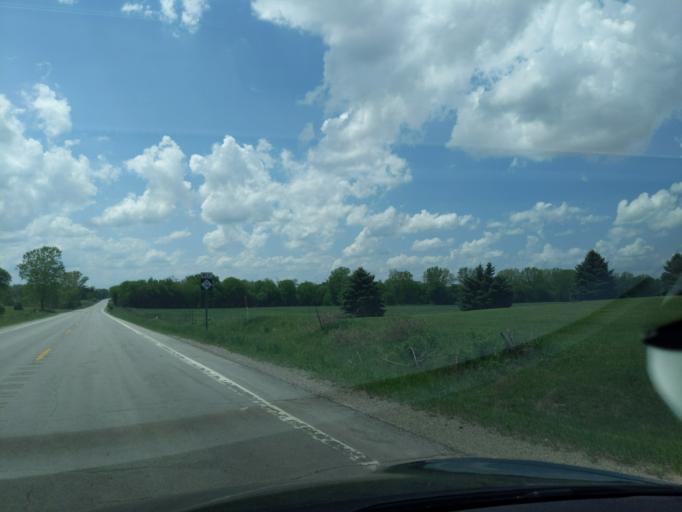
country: US
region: Michigan
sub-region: Ingham County
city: Stockbridge
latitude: 42.5561
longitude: -84.2591
